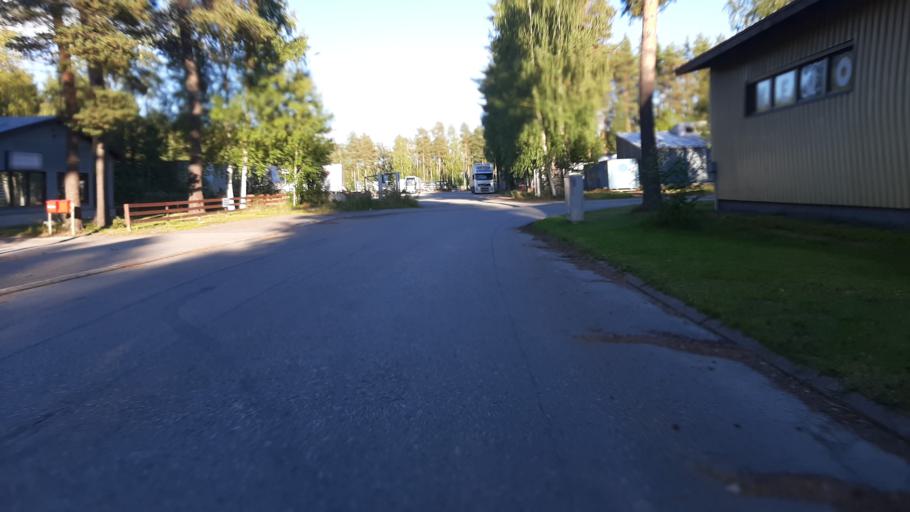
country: FI
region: North Karelia
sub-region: Joensuu
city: Joensuu
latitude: 62.6197
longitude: 29.7451
